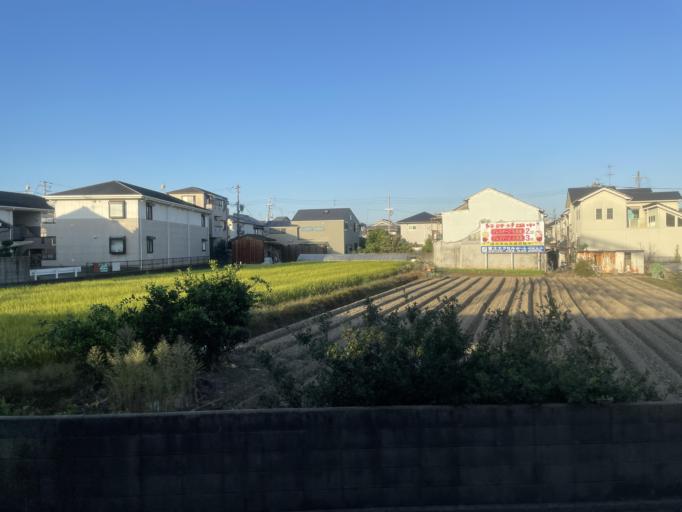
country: JP
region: Osaka
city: Matsubara
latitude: 34.5834
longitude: 135.5367
